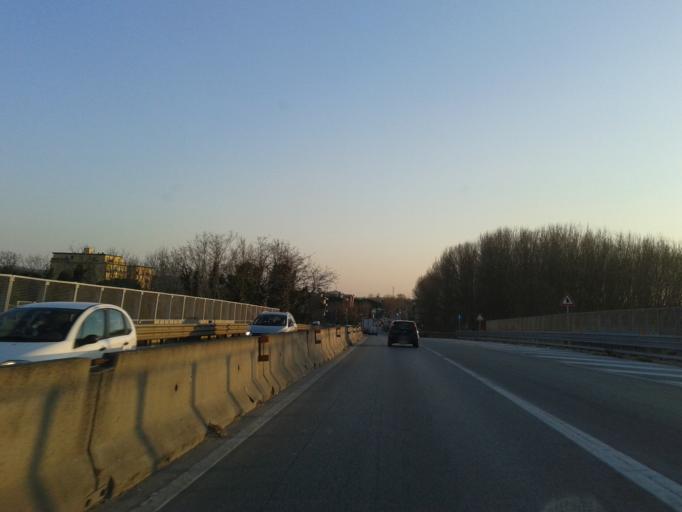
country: IT
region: Tuscany
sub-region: Provincia di Livorno
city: Livorno
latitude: 43.5949
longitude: 10.3497
